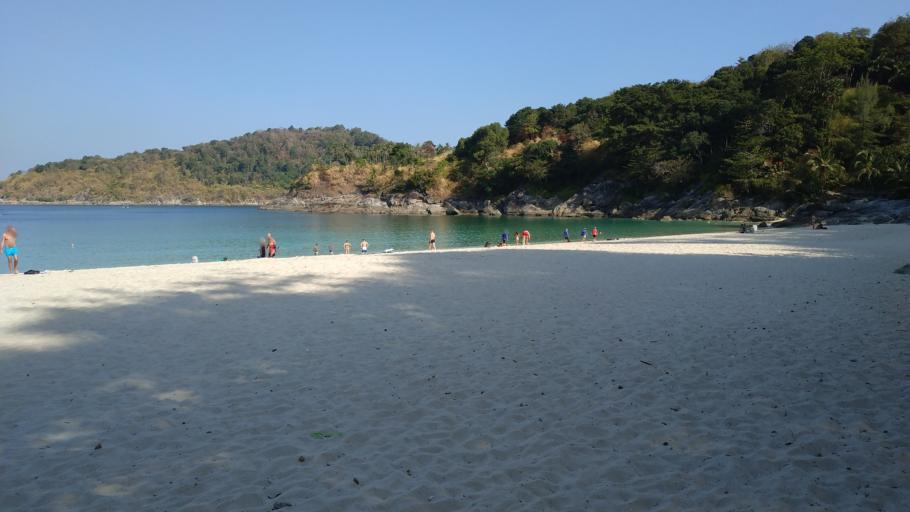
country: TH
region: Phuket
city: Patong
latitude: 7.8744
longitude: 98.2757
